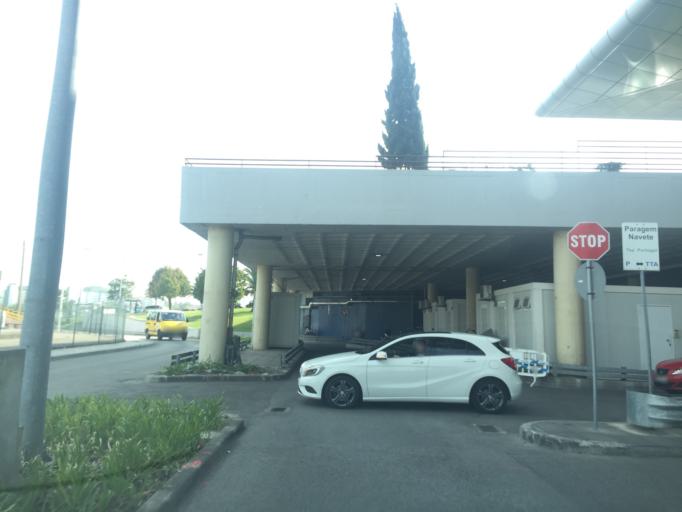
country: PT
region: Lisbon
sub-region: Loures
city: Moscavide
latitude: 38.7711
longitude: -9.1281
